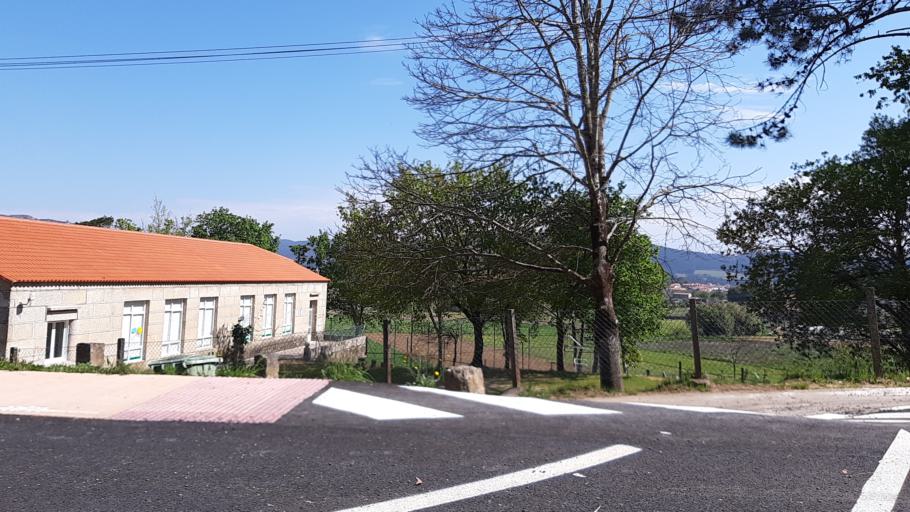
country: ES
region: Galicia
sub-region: Provincia de Pontevedra
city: O Rosal
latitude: 41.9302
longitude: -8.8527
